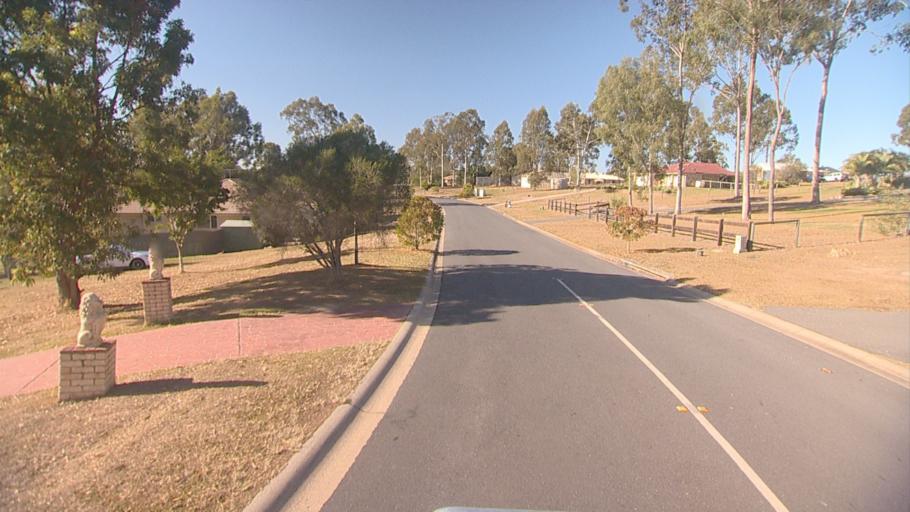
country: AU
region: Queensland
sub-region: Logan
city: Cedar Vale
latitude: -27.8642
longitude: 153.0365
